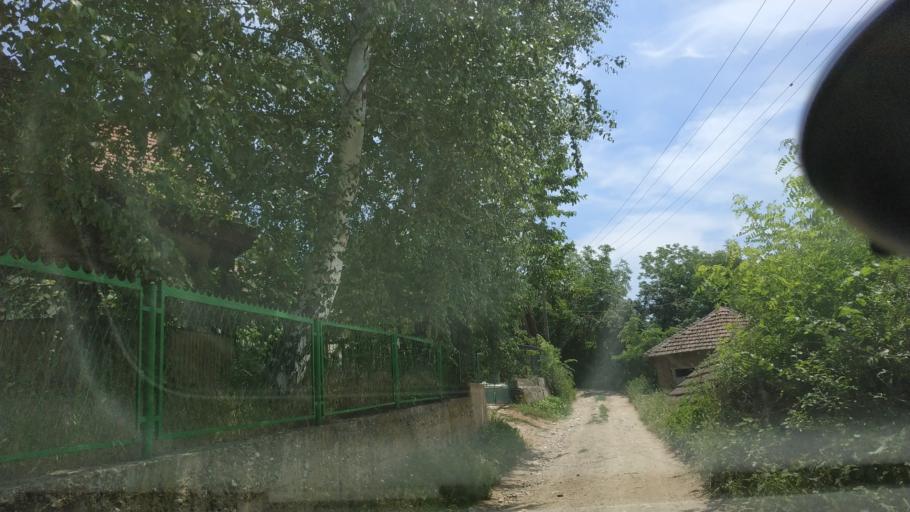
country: RS
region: Central Serbia
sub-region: Nisavski Okrug
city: Aleksinac
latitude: 43.5775
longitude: 21.7014
